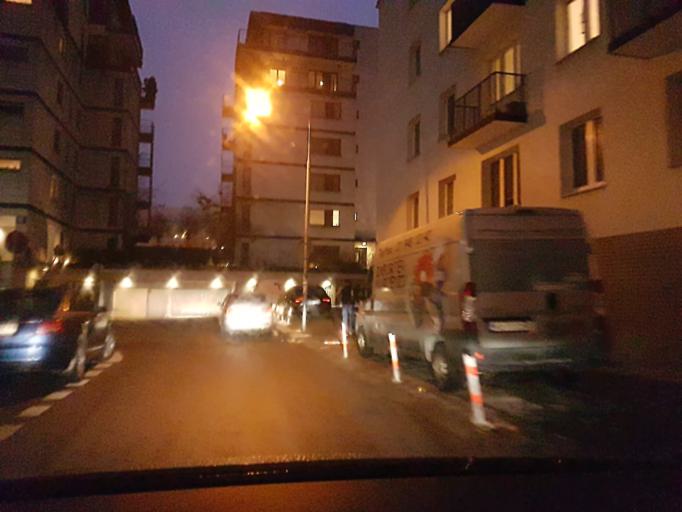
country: PL
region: Masovian Voivodeship
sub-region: Warszawa
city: Mokotow
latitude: 52.2045
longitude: 21.0194
